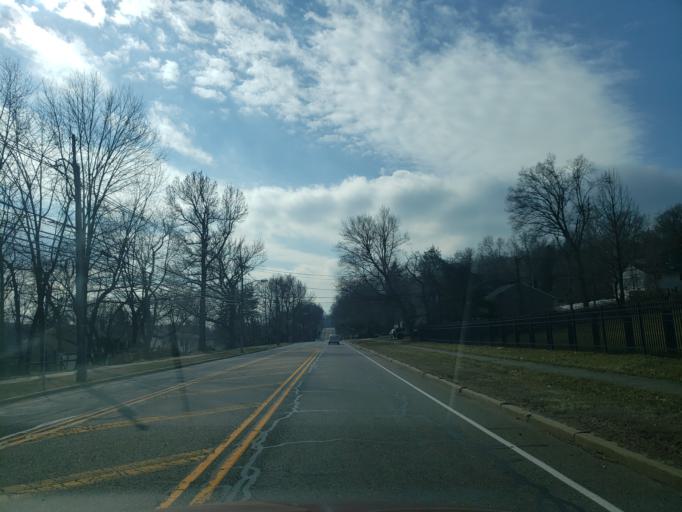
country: US
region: New Jersey
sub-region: Essex County
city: South Orange
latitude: 40.7806
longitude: -74.2773
